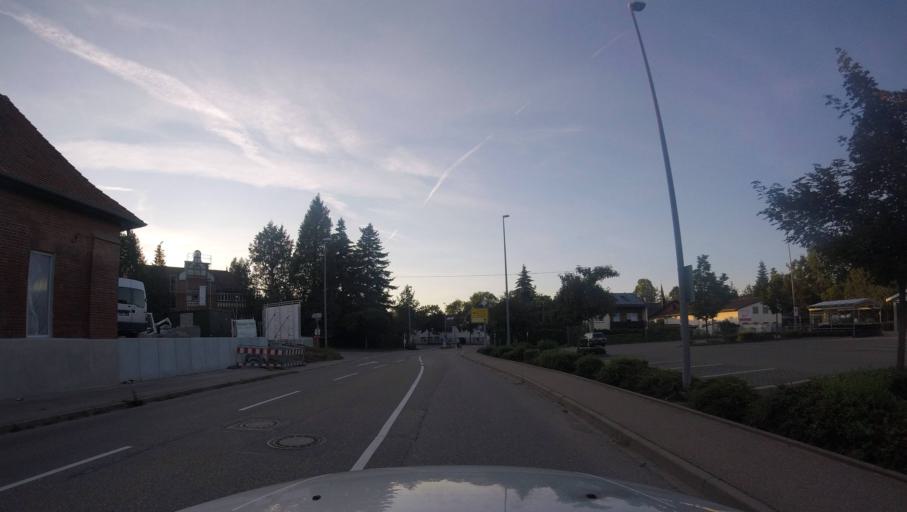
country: DE
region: Baden-Wuerttemberg
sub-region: Regierungsbezirk Stuttgart
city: Allmersbach im Tal
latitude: 48.9271
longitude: 9.4797
